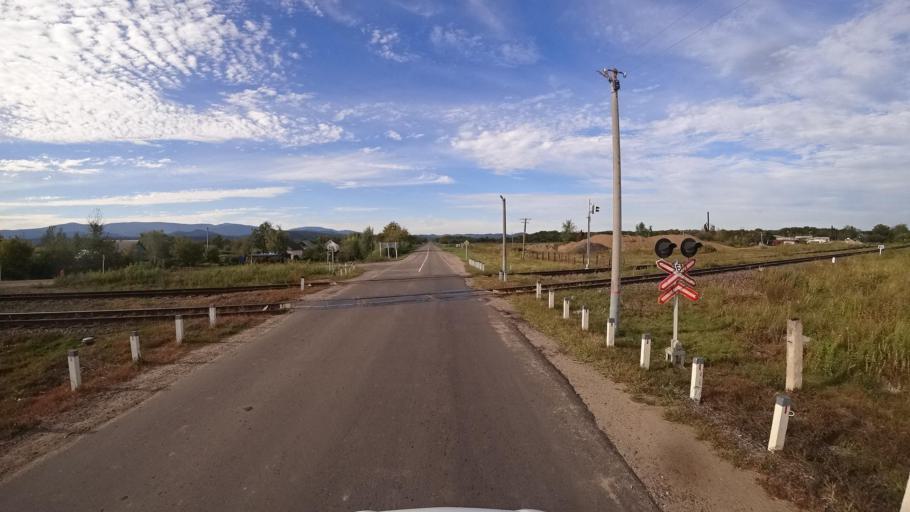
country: RU
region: Primorskiy
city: Dostoyevka
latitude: 44.2964
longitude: 133.4265
